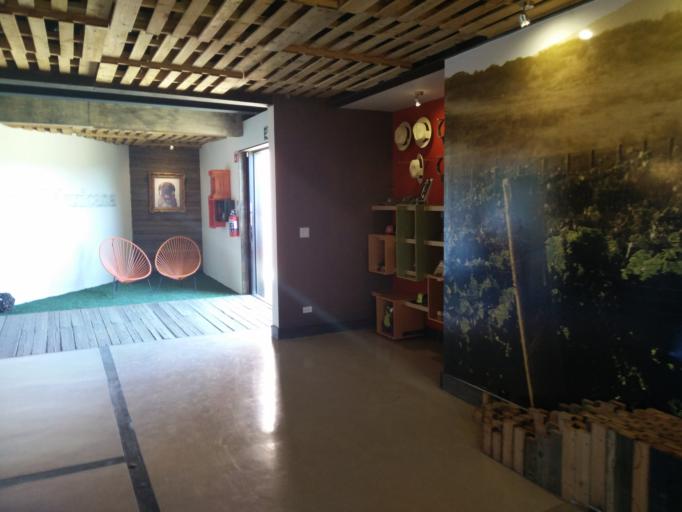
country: MX
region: Baja California
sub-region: Ensenada
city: Rancho Verde
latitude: 32.0170
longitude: -116.6638
